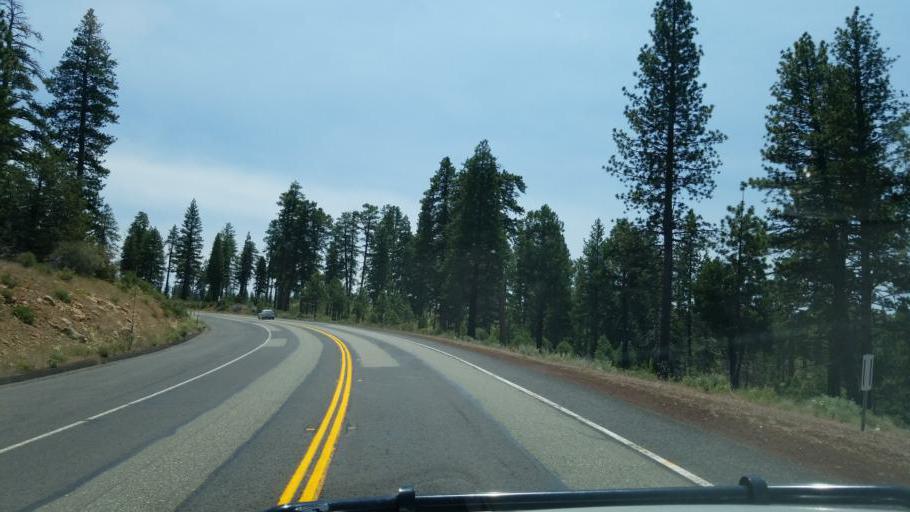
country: US
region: California
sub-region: Shasta County
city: Burney
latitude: 40.6976
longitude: -121.3920
